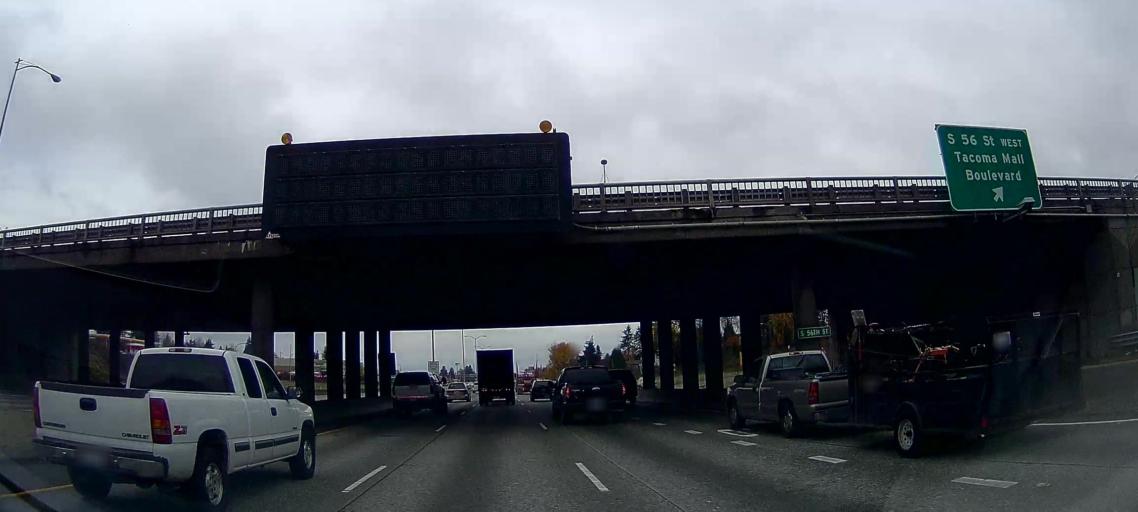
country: US
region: Washington
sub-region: Pierce County
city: Tacoma
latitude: 47.2067
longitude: -122.4619
